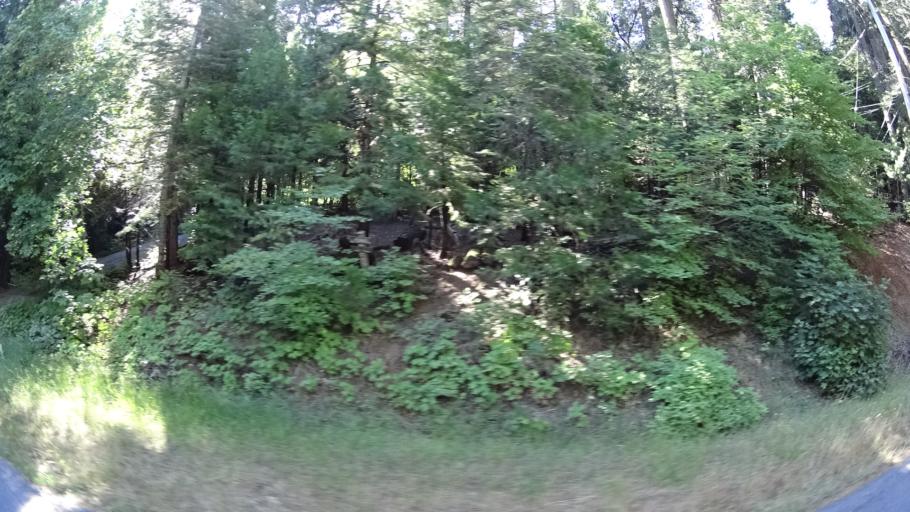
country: US
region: California
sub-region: Calaveras County
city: Arnold
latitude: 38.2573
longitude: -120.3176
